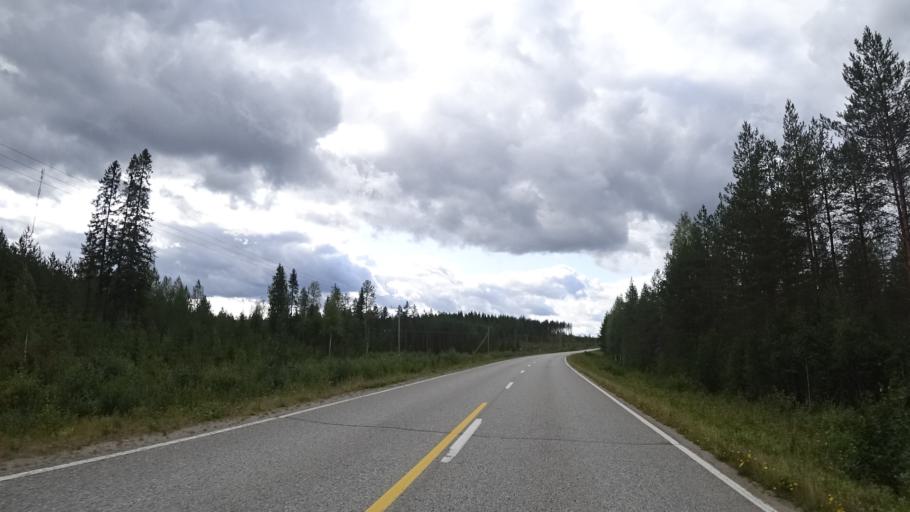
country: FI
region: North Karelia
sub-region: Joensuu
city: Ilomantsi
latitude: 62.6223
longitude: 31.2365
